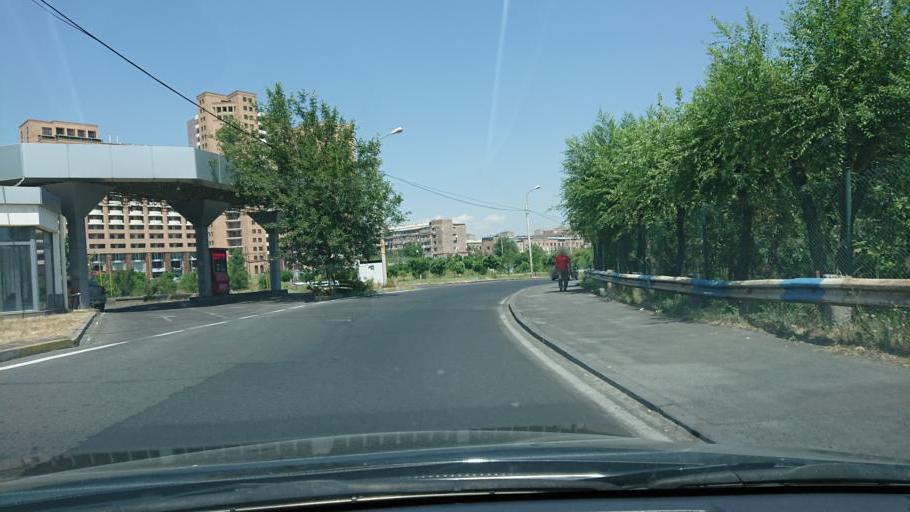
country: AM
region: Yerevan
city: Yerevan
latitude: 40.2120
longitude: 44.4916
